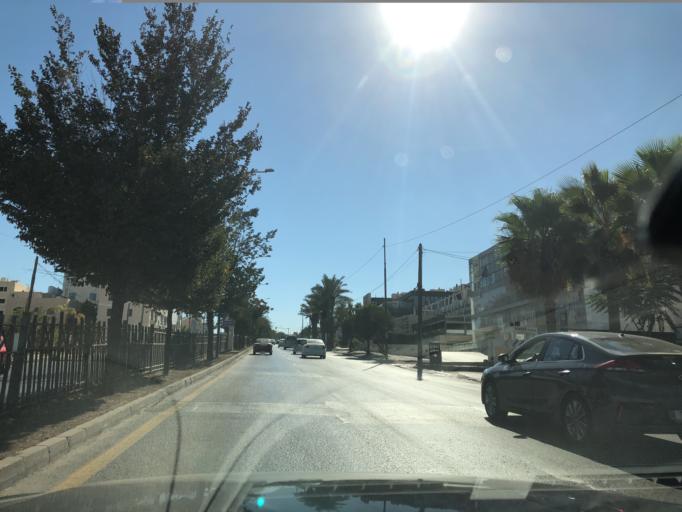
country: JO
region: Amman
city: Al Jubayhah
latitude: 31.9738
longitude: 35.8689
